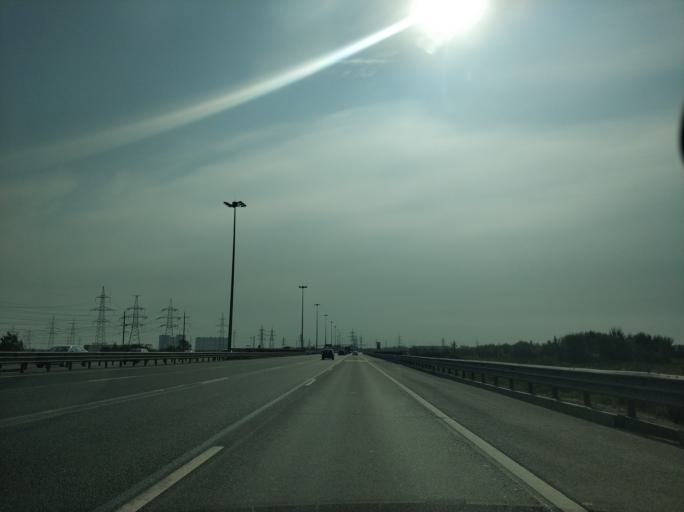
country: RU
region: Leningrad
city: Murino
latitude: 60.0257
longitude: 30.4497
